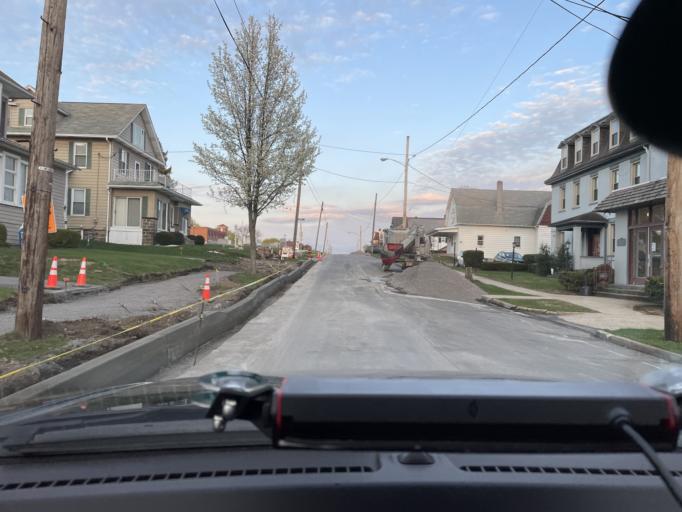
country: US
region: Pennsylvania
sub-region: Cambria County
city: Ebensburg
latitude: 40.4878
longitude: -78.7288
